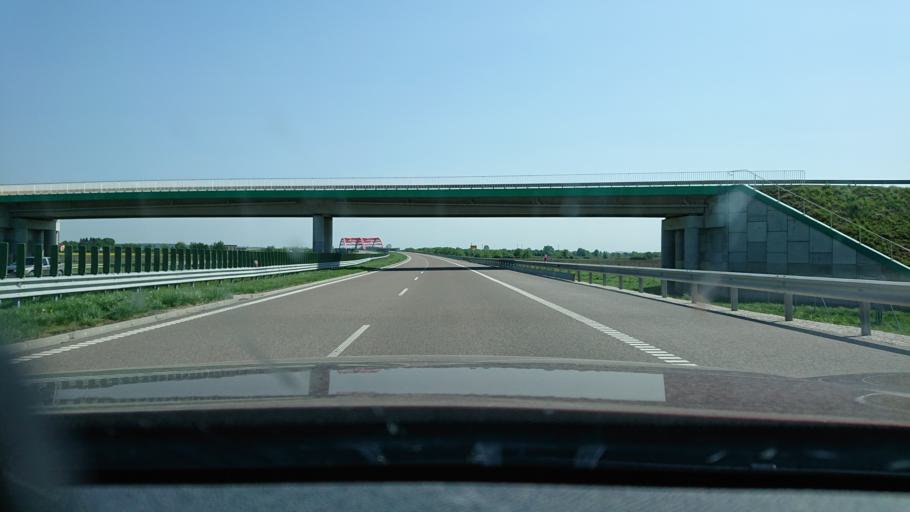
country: PL
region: Subcarpathian Voivodeship
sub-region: Powiat przemyski
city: Stubno
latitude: 49.9300
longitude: 22.9187
